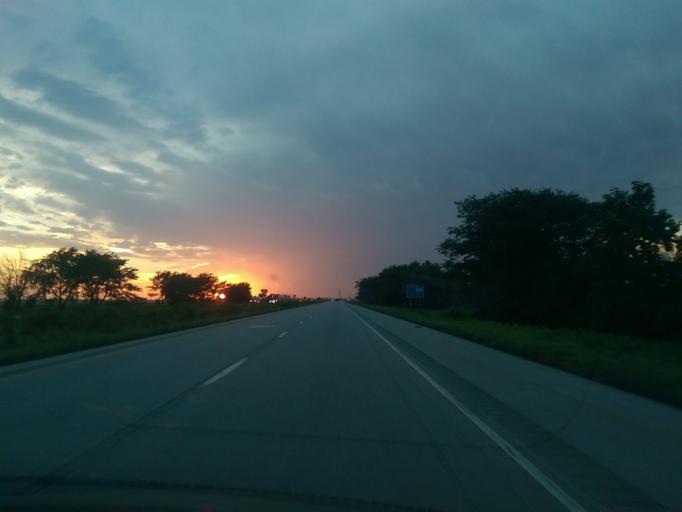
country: US
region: Iowa
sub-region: Fremont County
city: Hamburg
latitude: 40.5904
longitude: -95.6641
